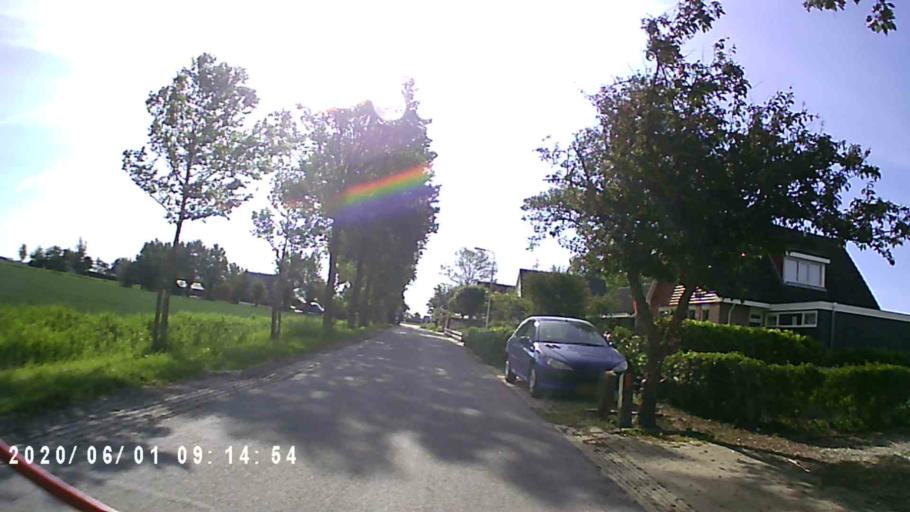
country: NL
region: Friesland
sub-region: Gemeente Leeuwarderadeel
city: Stiens
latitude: 53.2779
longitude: 5.7593
